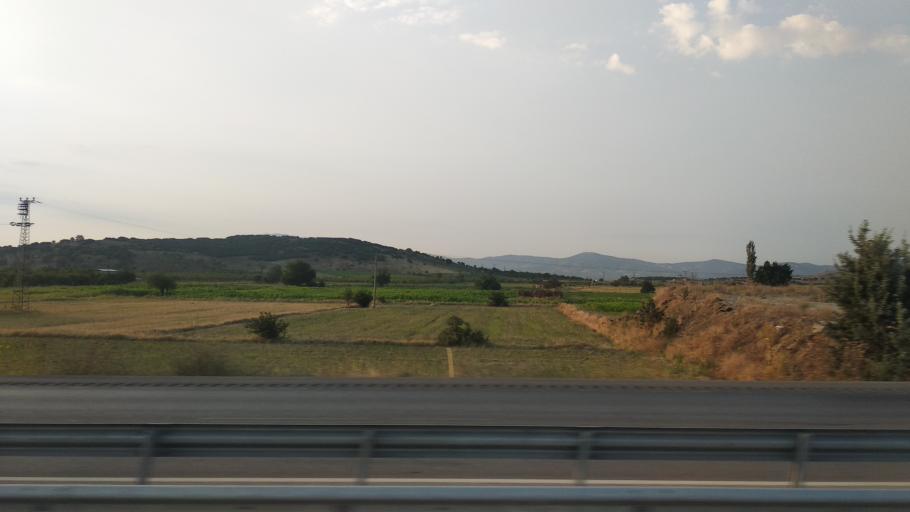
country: TR
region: Manisa
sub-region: Kula
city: Kula
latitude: 38.5531
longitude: 28.6868
